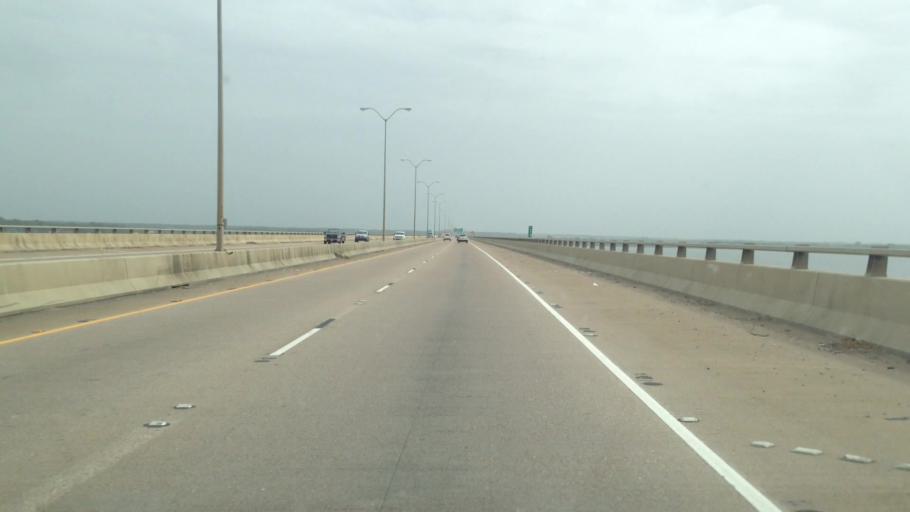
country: US
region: Louisiana
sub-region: Caddo Parish
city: Shreveport
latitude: 32.4988
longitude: -93.8194
